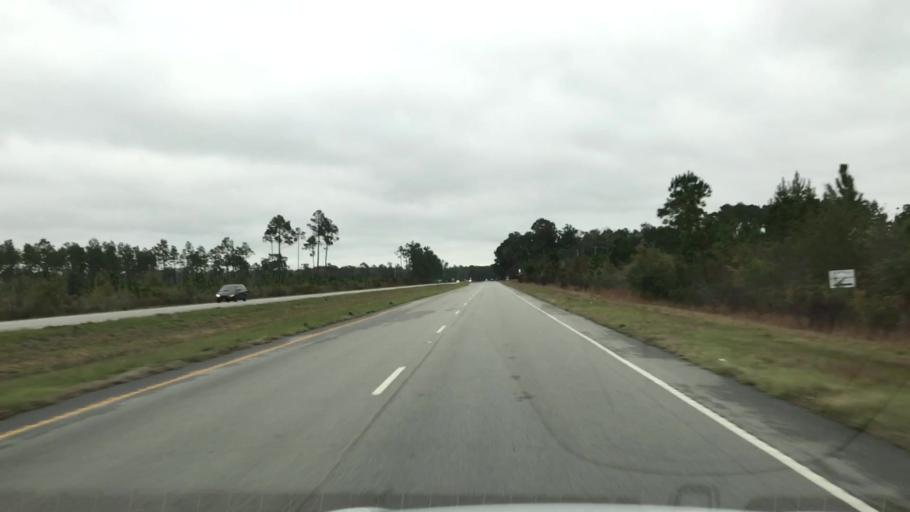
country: US
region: South Carolina
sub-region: Charleston County
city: Awendaw
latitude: 33.1707
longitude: -79.4192
